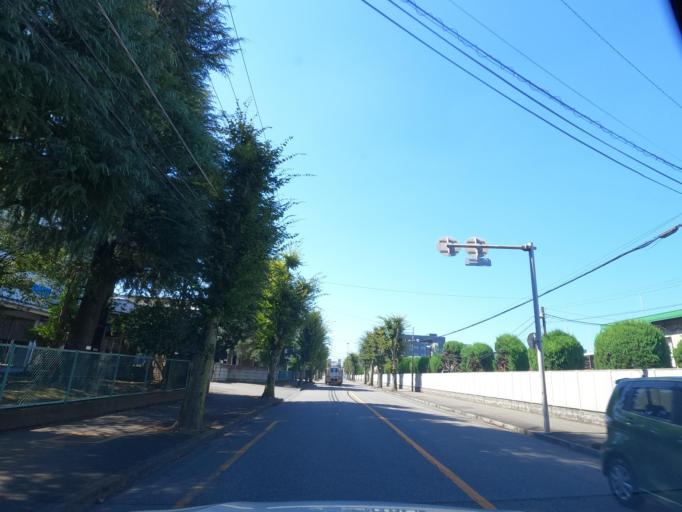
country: JP
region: Saitama
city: Kawagoe
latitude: 35.8890
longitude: 139.4497
